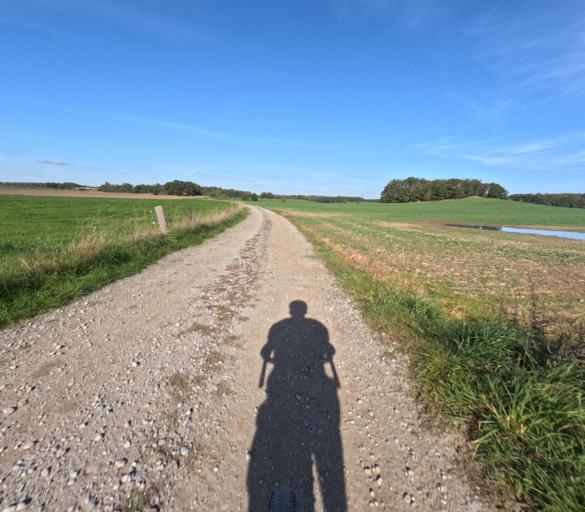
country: DE
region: Saxony
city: Radeburg
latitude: 51.1690
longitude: 13.7582
